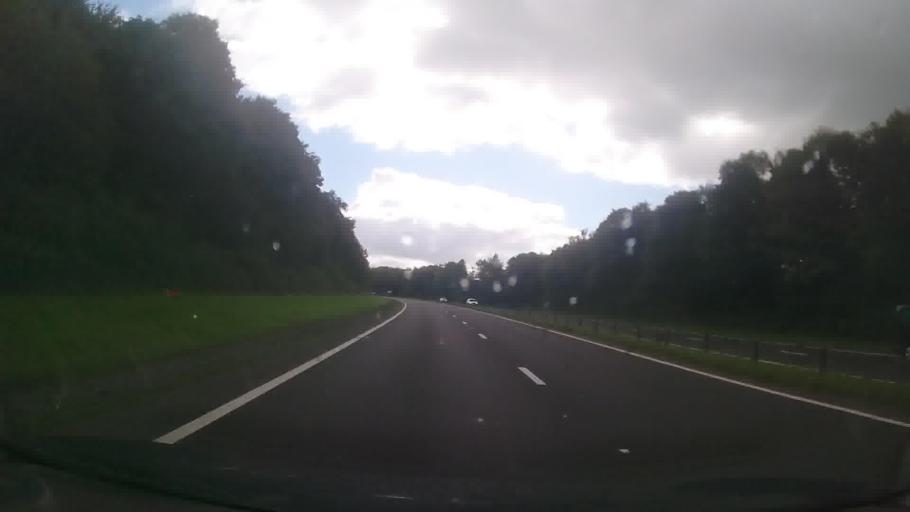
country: GB
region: Wales
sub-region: Carmarthenshire
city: Carmarthen
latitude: 51.8431
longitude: -4.3019
